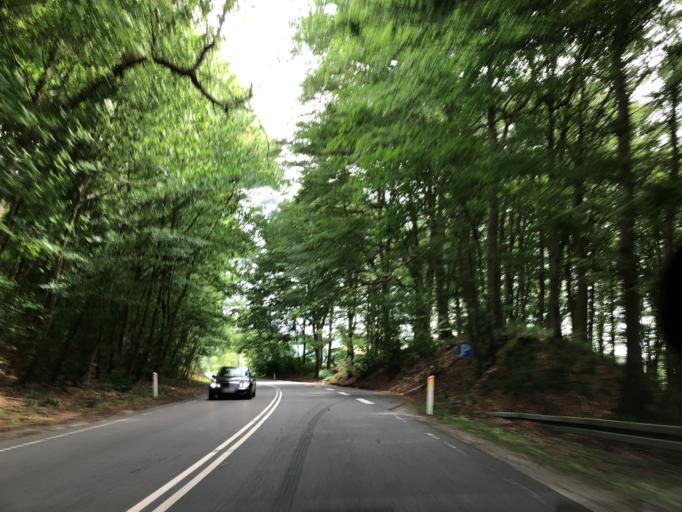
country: DK
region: Central Jutland
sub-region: Skanderborg Kommune
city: Skanderborg
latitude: 56.0610
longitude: 9.9025
